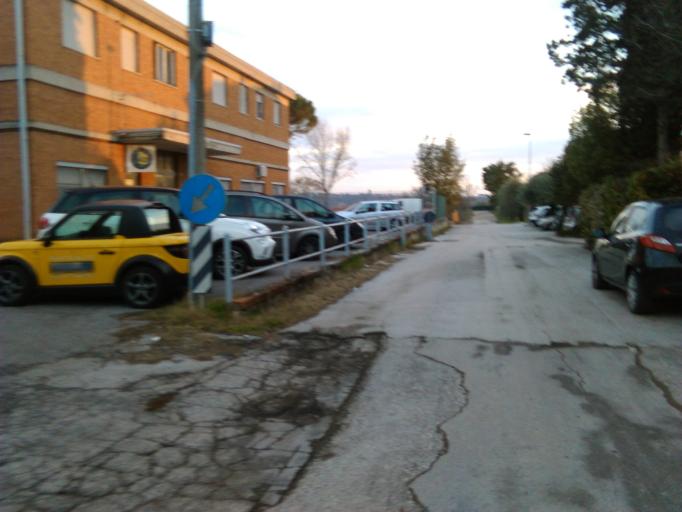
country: IT
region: Umbria
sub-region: Provincia di Perugia
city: Lacugnano
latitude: 43.0916
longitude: 12.3606
